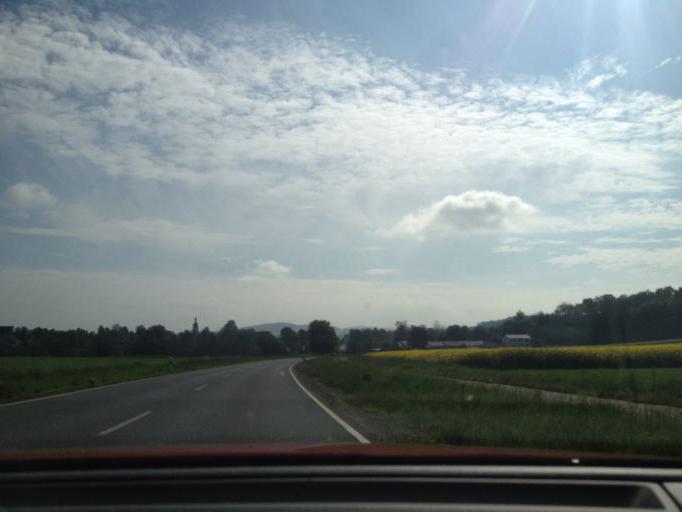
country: DE
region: Bavaria
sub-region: Upper Palatinate
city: Waldershof
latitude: 49.9752
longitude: 12.0509
